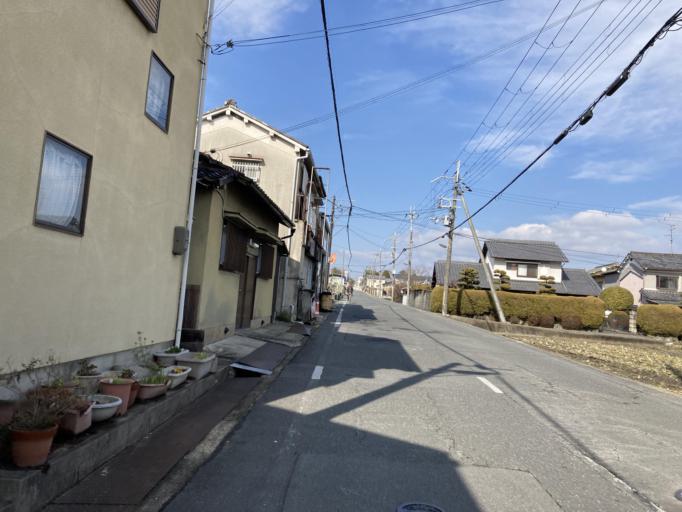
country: JP
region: Nara
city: Nara-shi
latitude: 34.6943
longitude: 135.8065
